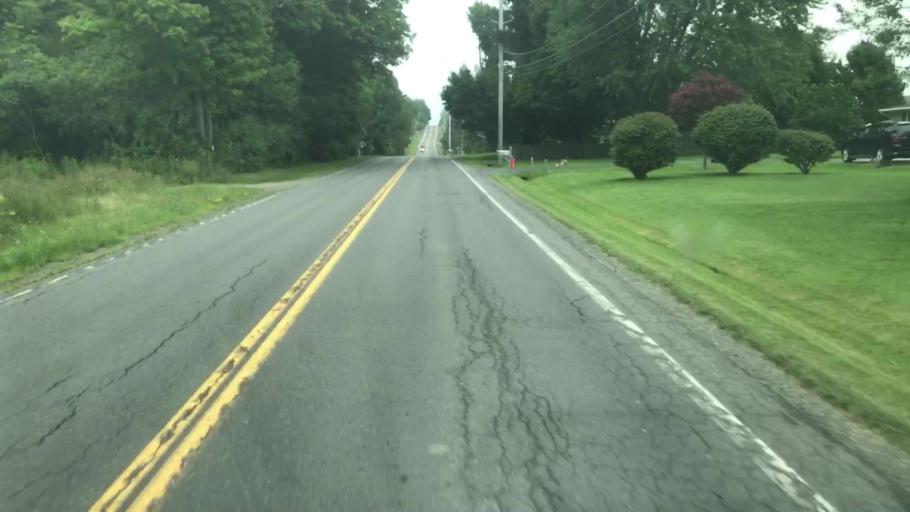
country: US
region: New York
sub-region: Onondaga County
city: Skaneateles
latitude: 42.9582
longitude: -76.4648
